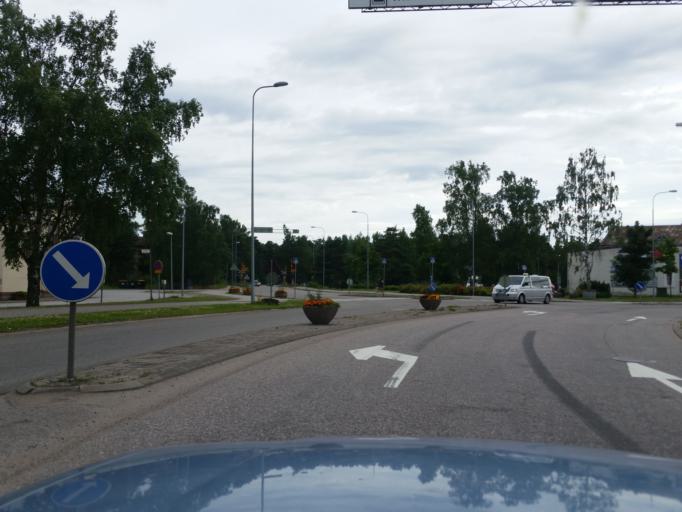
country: FI
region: Uusimaa
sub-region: Raaseporin
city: Hanko
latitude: 59.8320
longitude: 22.9902
